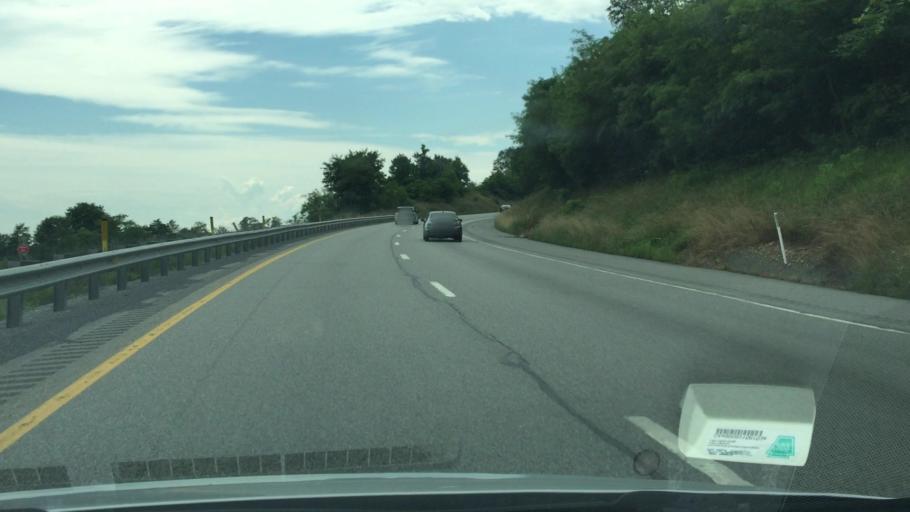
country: US
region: Pennsylvania
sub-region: Bedford County
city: Earlston
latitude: 39.8845
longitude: -78.2441
